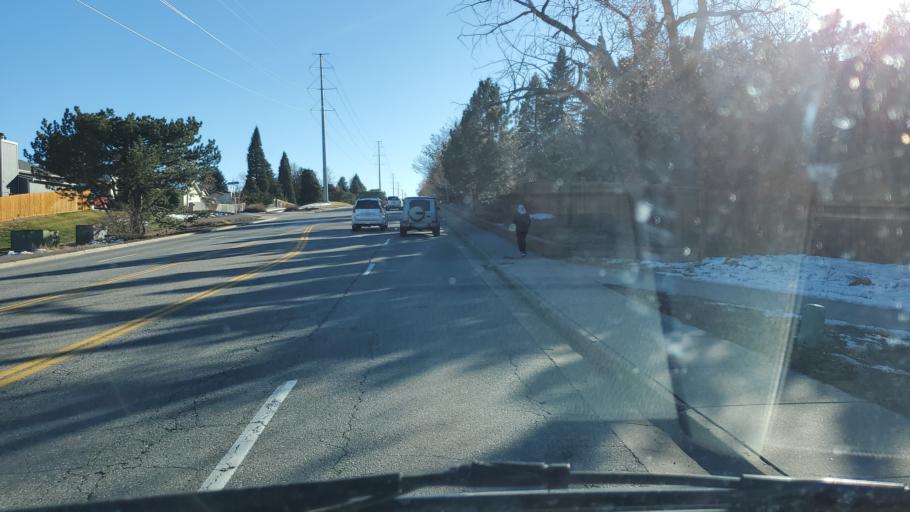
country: US
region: Colorado
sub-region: Arapahoe County
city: Castlewood
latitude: 39.5765
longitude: -104.9044
